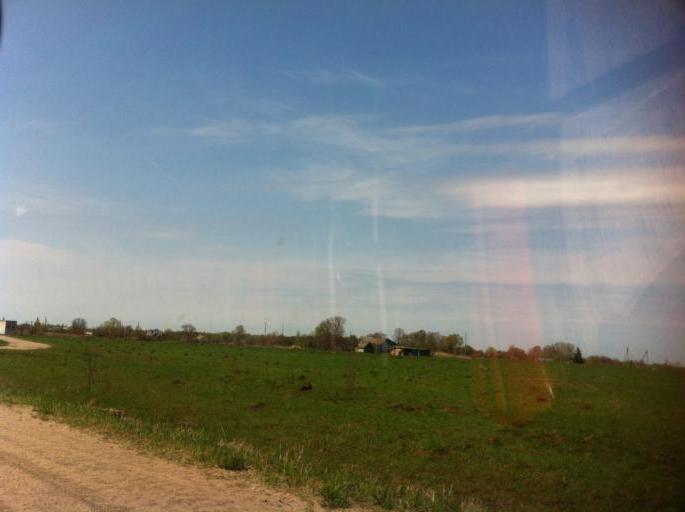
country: RU
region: Pskov
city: Izborsk
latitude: 57.8376
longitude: 28.0654
